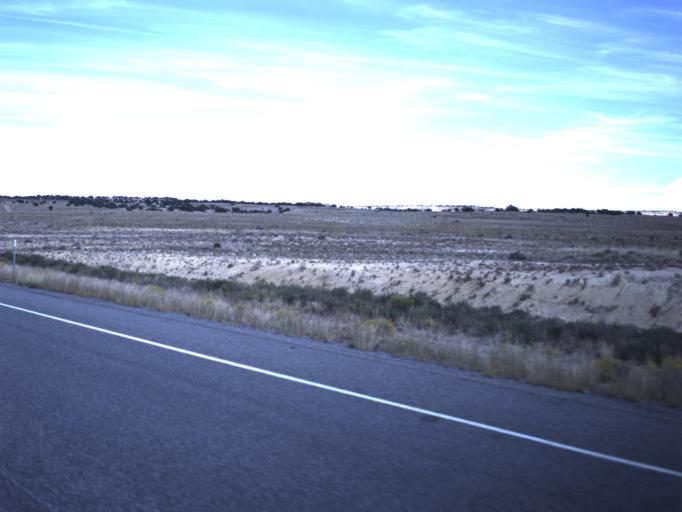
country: US
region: Utah
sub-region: Emery County
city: Castle Dale
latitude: 38.8829
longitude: -110.6557
